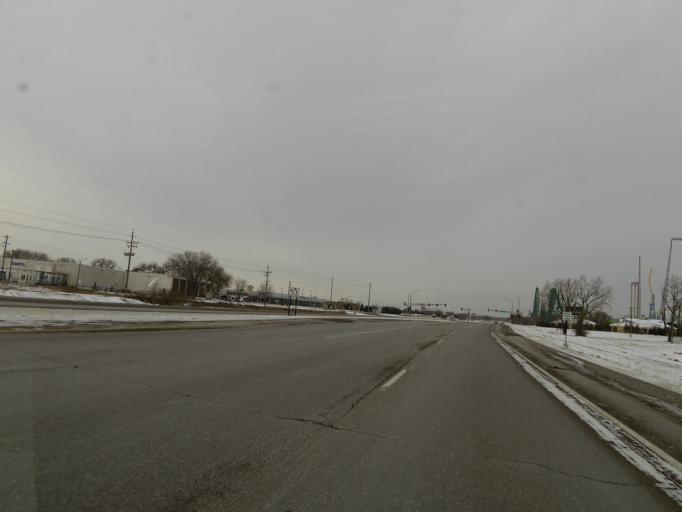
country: US
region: Minnesota
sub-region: Hennepin County
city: Eden Prairie
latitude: 44.7958
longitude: -93.4474
